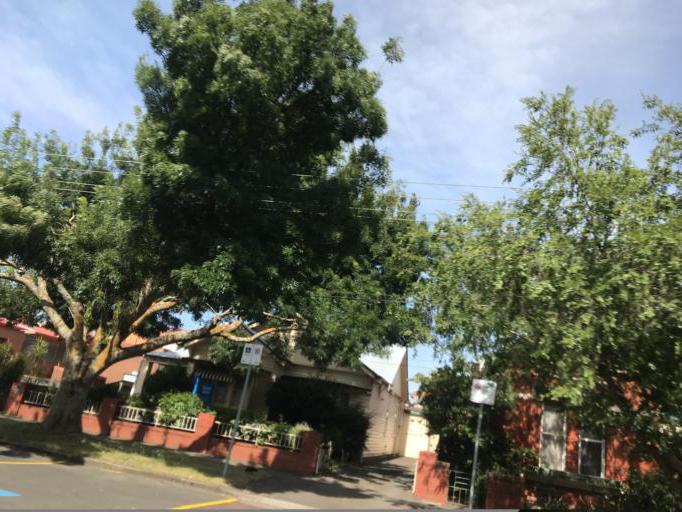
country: AU
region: Victoria
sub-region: Ballarat North
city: Ballarat Central
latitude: -37.5619
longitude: 143.8503
